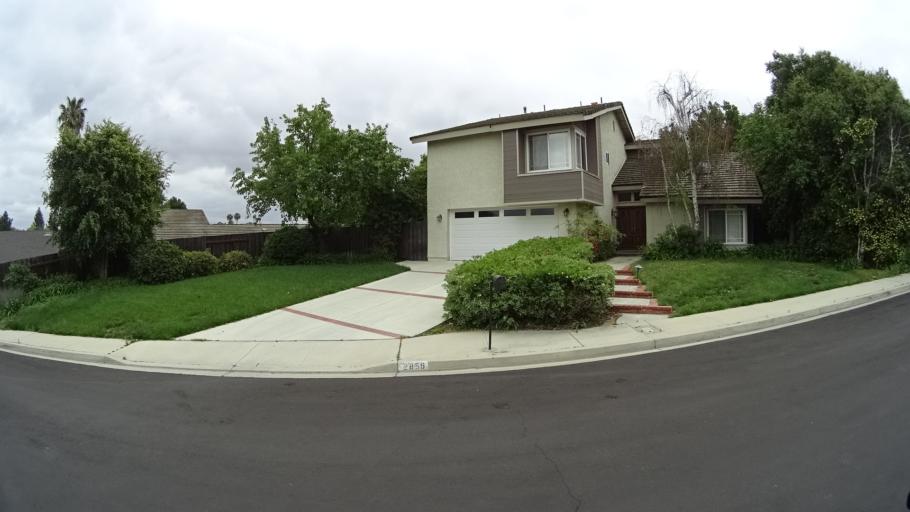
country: US
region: California
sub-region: Ventura County
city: Thousand Oaks
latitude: 34.2188
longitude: -118.8838
